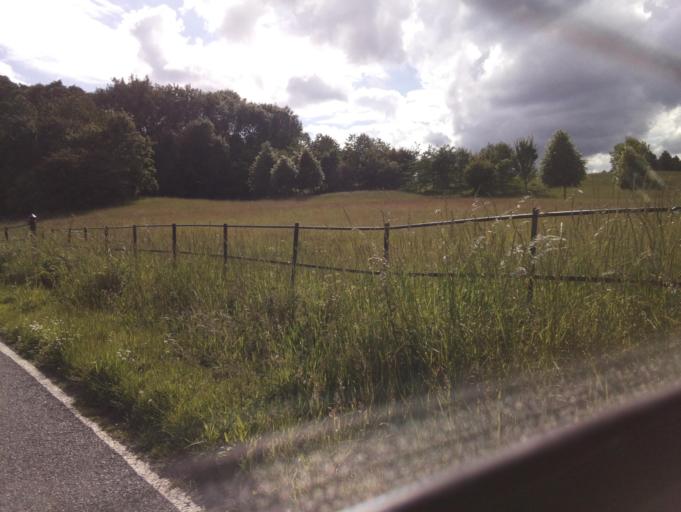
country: GB
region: England
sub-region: Hertfordshire
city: Abbots Langley
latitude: 51.6742
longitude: -0.4297
